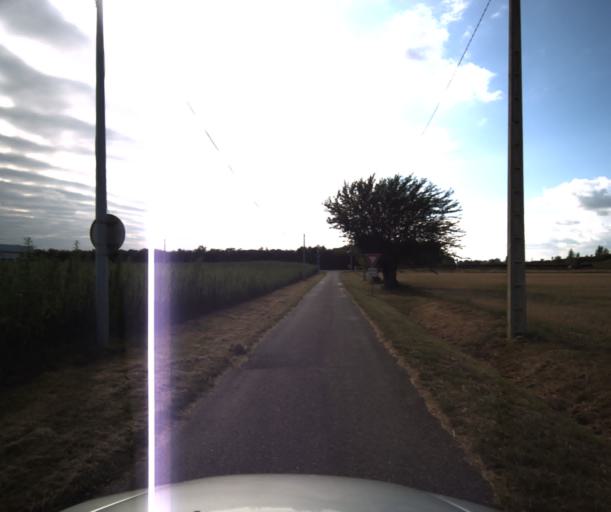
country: FR
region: Midi-Pyrenees
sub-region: Departement de la Haute-Garonne
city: Le Fauga
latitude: 43.4298
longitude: 1.3086
